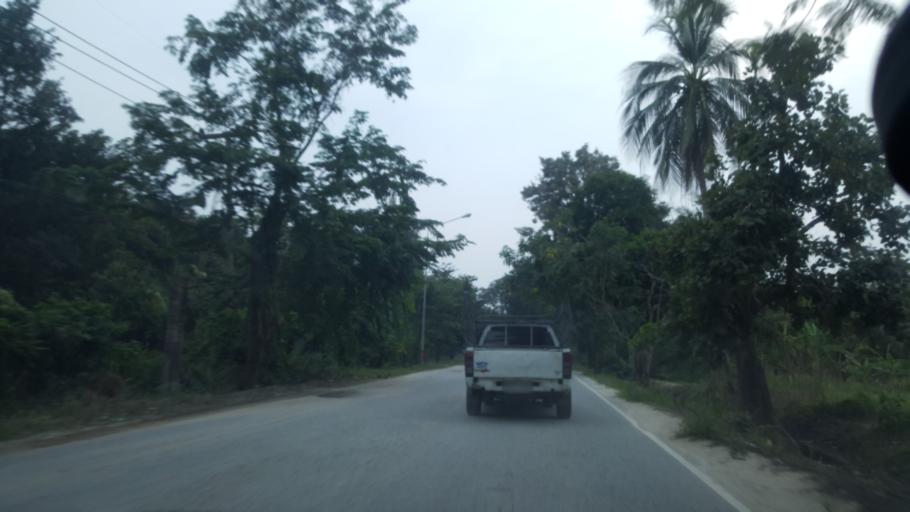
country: TH
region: Chon Buri
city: Si Racha
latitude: 13.2373
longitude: 101.0205
